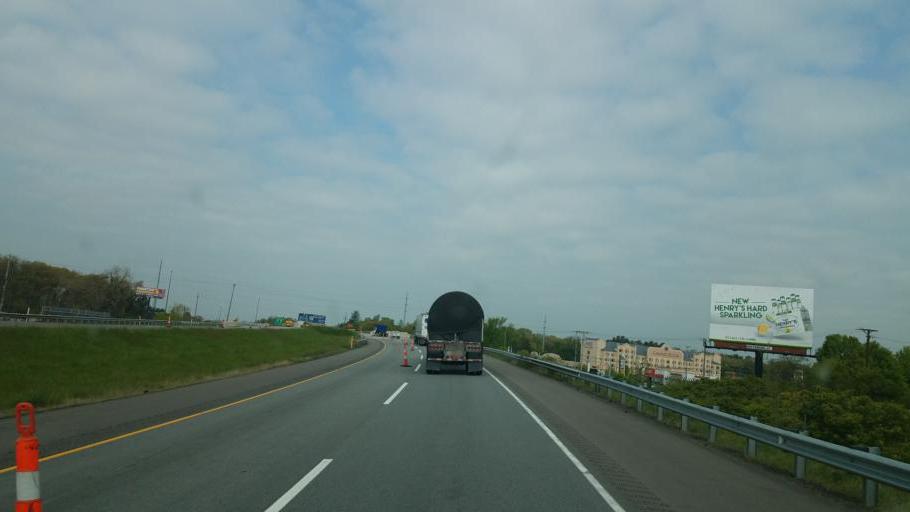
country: US
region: Indiana
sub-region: Saint Joseph County
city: Georgetown
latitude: 41.7221
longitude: -86.2480
